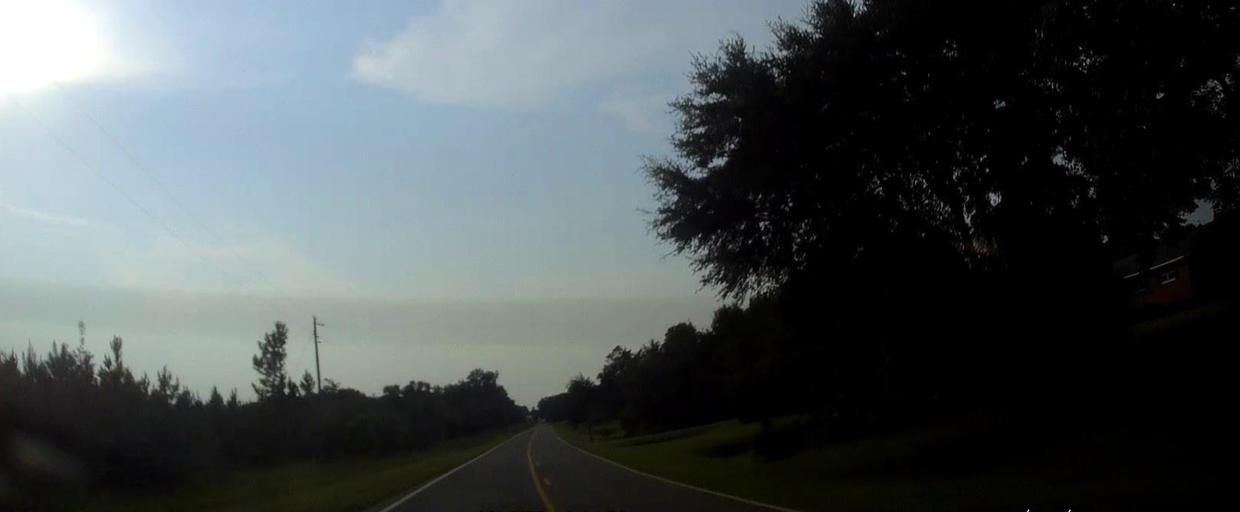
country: US
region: Georgia
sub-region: Laurens County
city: Dublin
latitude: 32.4860
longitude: -82.9748
